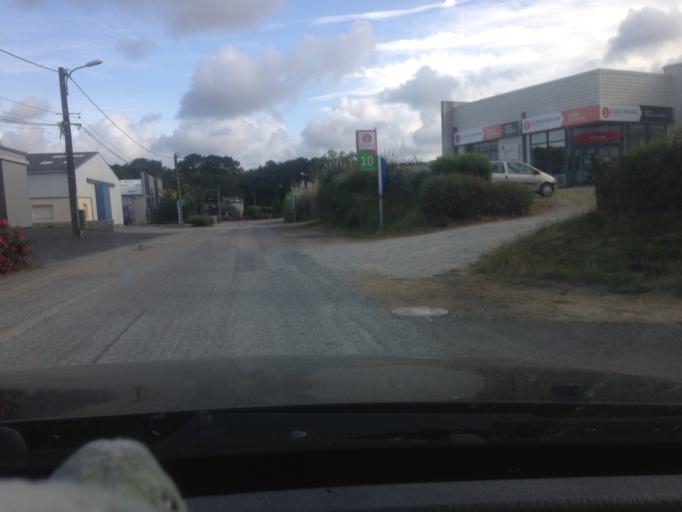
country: FR
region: Brittany
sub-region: Departement du Morbihan
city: Carnac
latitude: 47.5891
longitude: -3.0586
